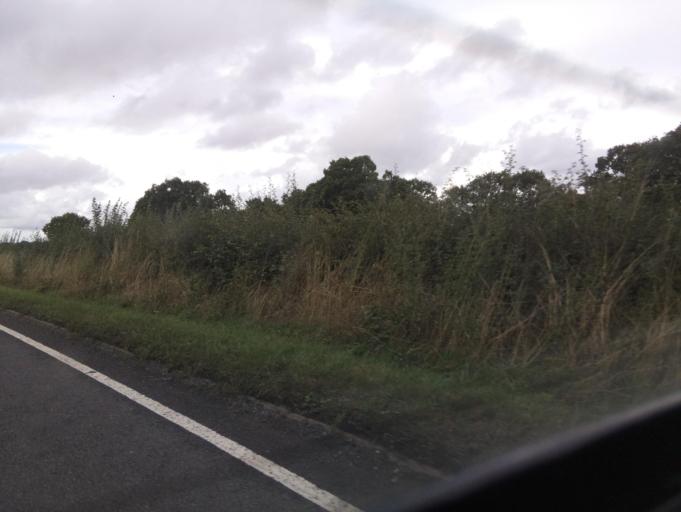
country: GB
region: England
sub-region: Worcestershire
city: Droitwich
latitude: 52.2946
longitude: -2.1713
